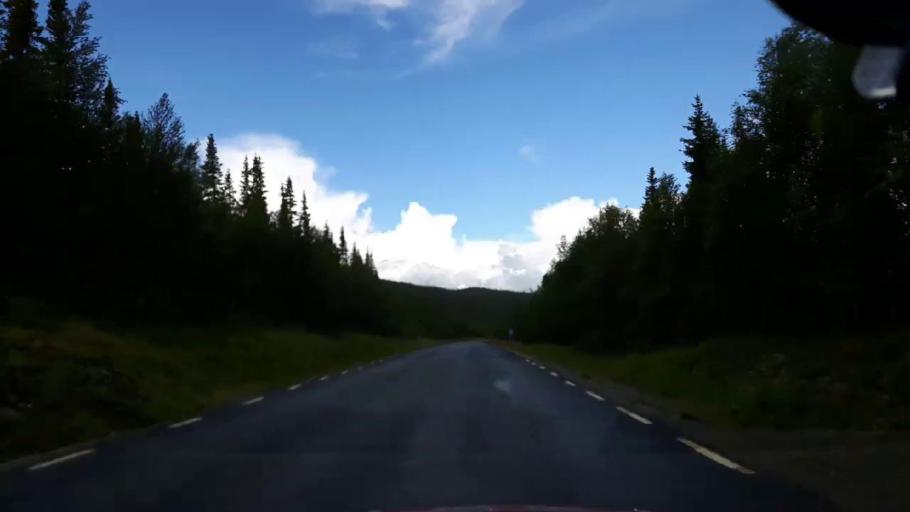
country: SE
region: Vaesterbotten
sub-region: Vilhelmina Kommun
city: Sjoberg
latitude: 65.0089
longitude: 15.1815
